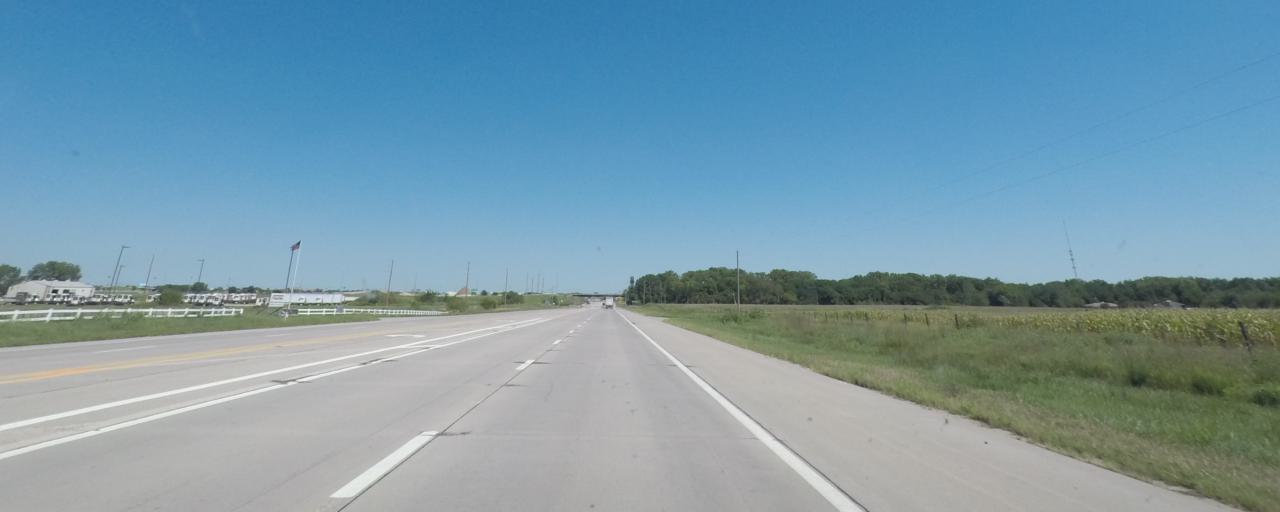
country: US
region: Kansas
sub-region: Lyon County
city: Emporia
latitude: 38.4122
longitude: -96.2487
